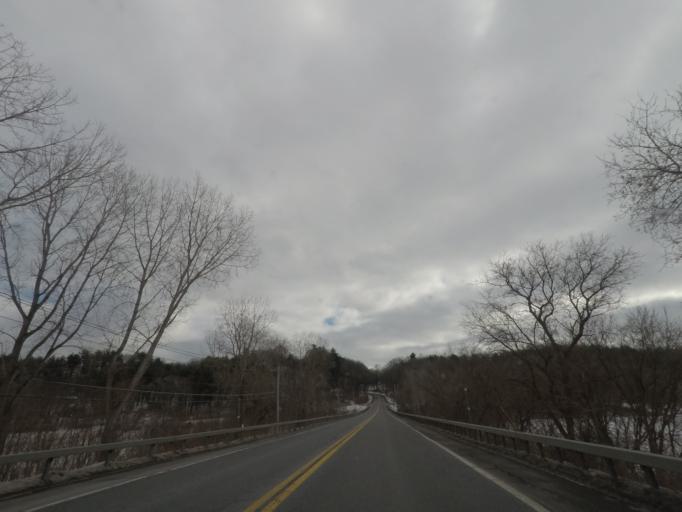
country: US
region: New York
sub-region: Saratoga County
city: Schuylerville
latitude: 43.0973
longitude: -73.5700
